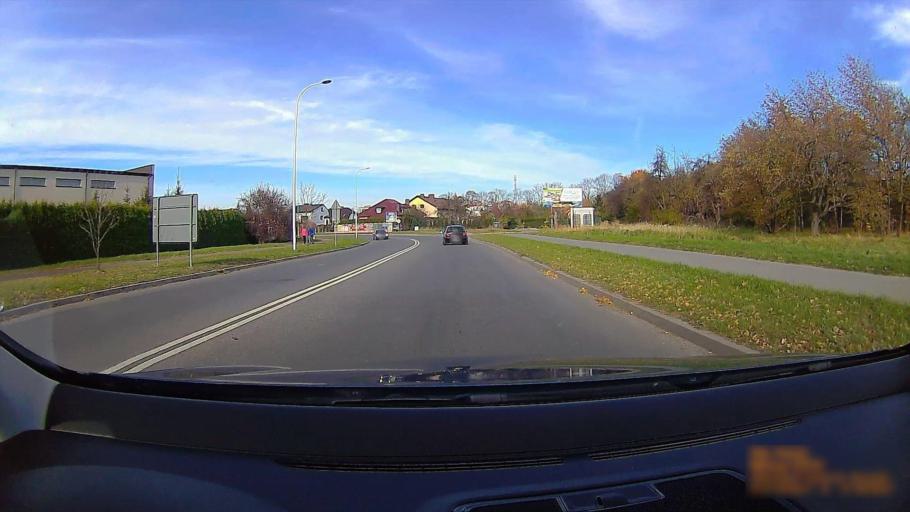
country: PL
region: Greater Poland Voivodeship
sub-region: Powiat ostrzeszowski
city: Ostrzeszow
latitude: 51.4278
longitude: 17.9387
